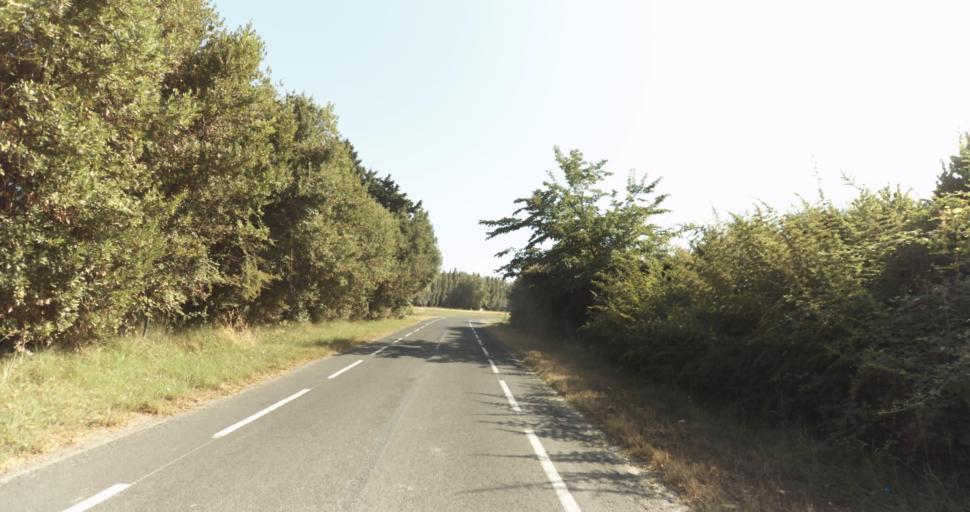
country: FR
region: Languedoc-Roussillon
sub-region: Departement des Pyrenees-Orientales
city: Latour-Bas-Elne
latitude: 42.6292
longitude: 3.0062
